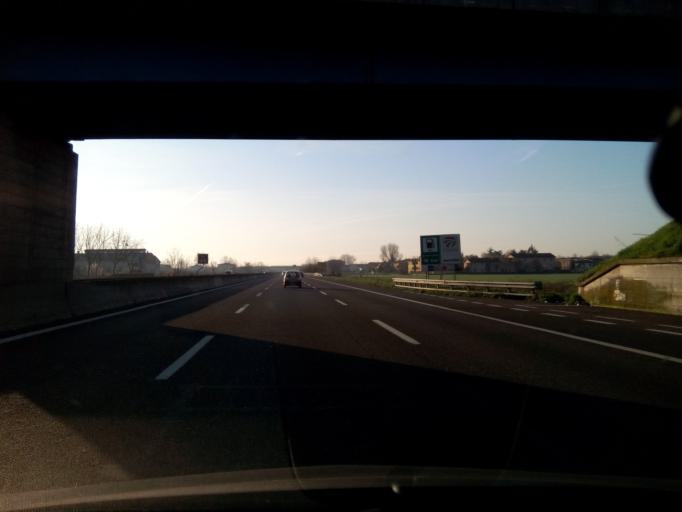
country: IT
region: Lombardy
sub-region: Provincia di Lodi
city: Guardamiglio
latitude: 45.1164
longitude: 9.6786
